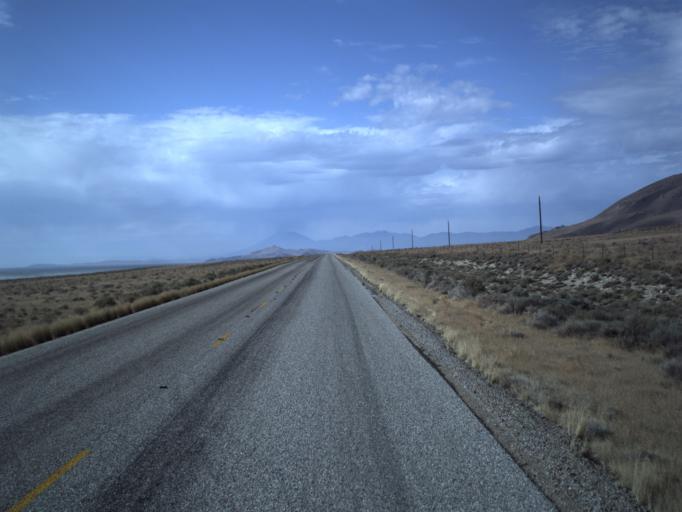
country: US
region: Utah
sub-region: Tooele County
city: Wendover
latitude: 41.4950
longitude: -113.6140
